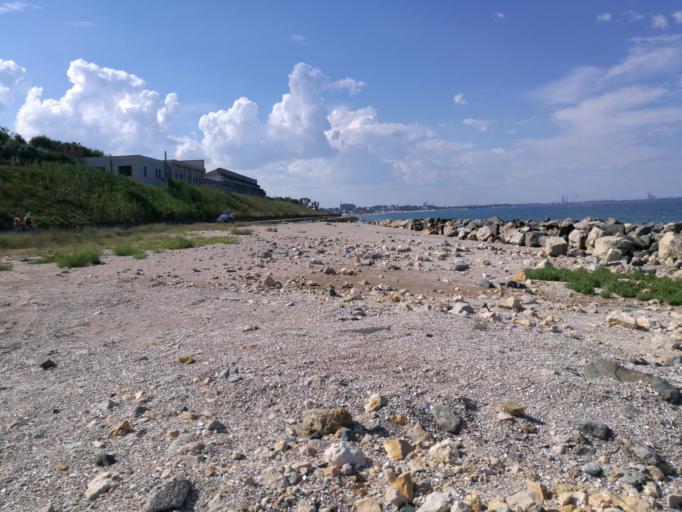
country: RO
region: Constanta
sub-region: Oras Eforie
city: Eforie
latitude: 44.0400
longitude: 28.6495
